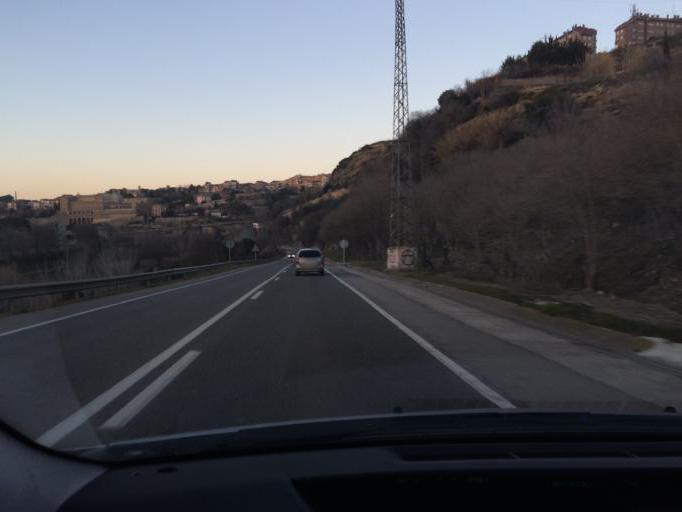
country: ES
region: Catalonia
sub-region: Provincia de Barcelona
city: Manresa
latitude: 41.7146
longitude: 1.8324
